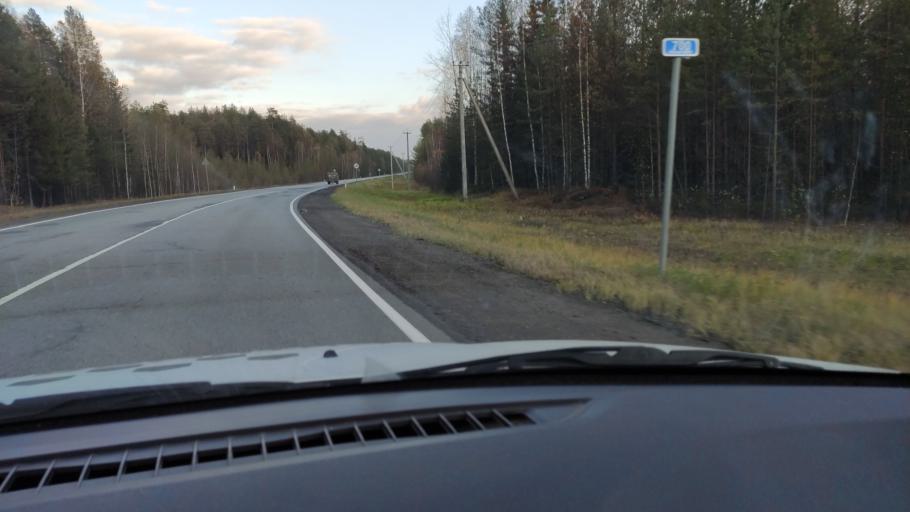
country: RU
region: Kirov
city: Belaya Kholunitsa
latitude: 58.9087
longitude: 50.9863
